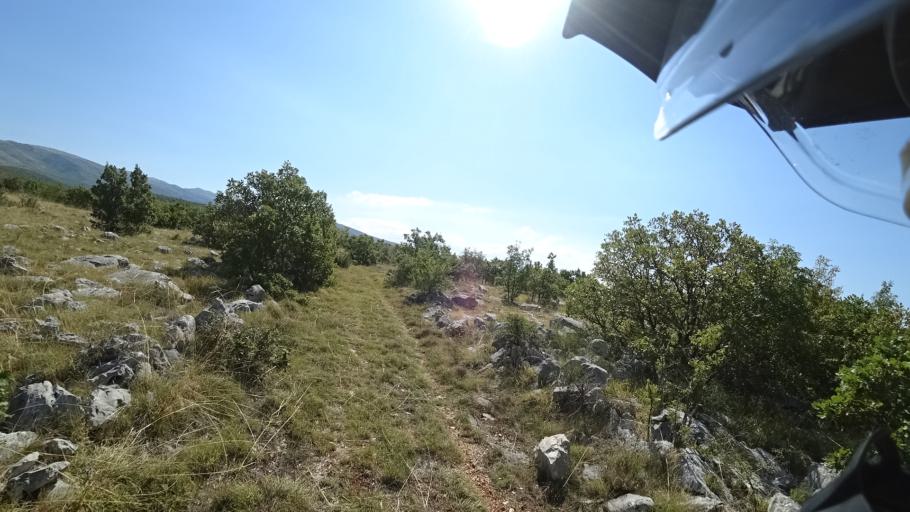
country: HR
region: Sibensko-Kniniska
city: Drnis
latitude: 43.8612
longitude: 16.2700
